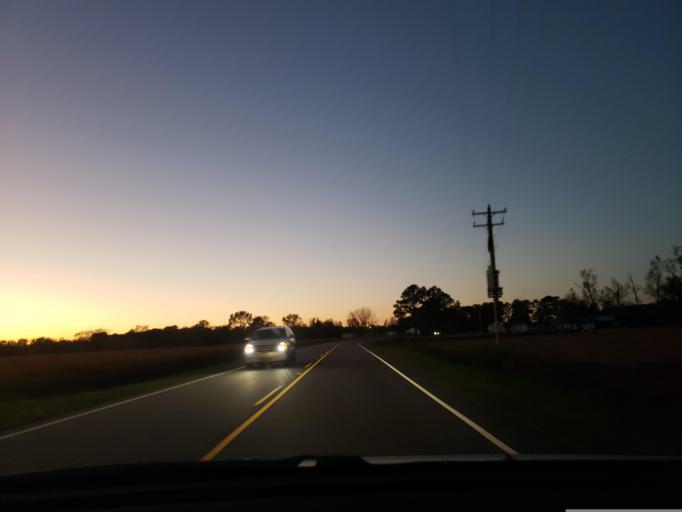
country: US
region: North Carolina
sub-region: Duplin County
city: Kenansville
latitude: 34.9093
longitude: -77.9272
